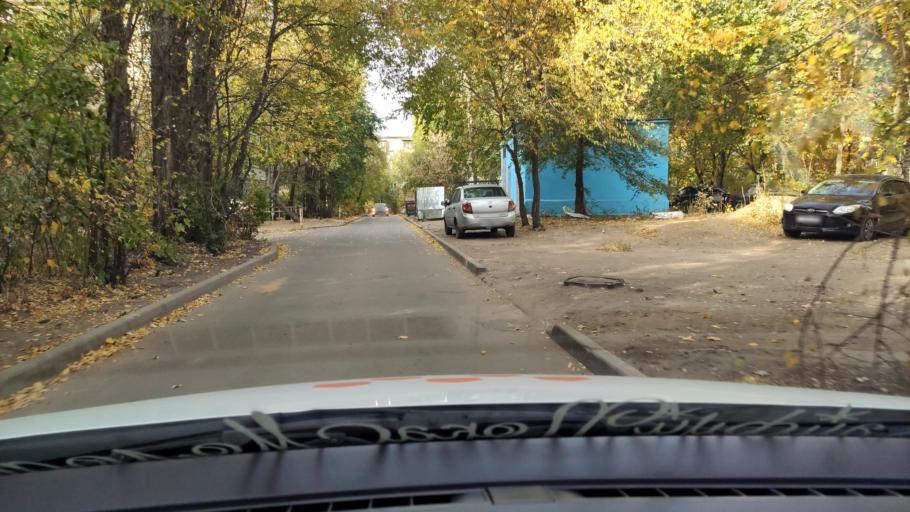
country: RU
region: Voronezj
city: Voronezh
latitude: 51.6482
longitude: 39.1341
